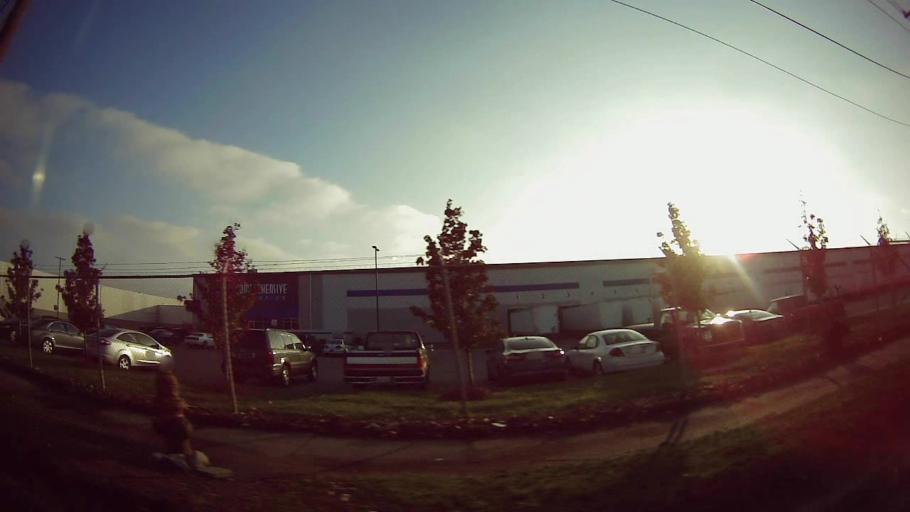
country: US
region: Michigan
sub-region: Wayne County
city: Dearborn
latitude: 42.3332
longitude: -83.1567
